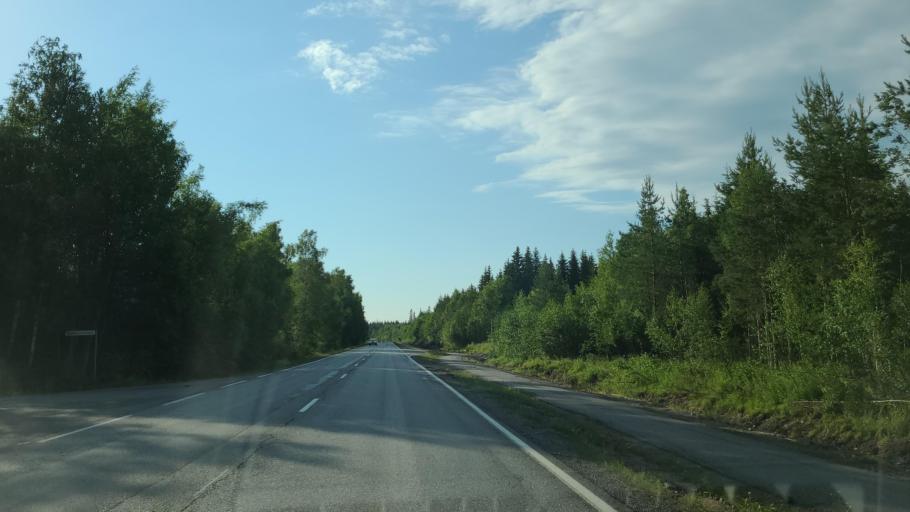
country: FI
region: Ostrobothnia
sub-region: Vaasa
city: Replot
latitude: 63.2008
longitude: 21.5326
